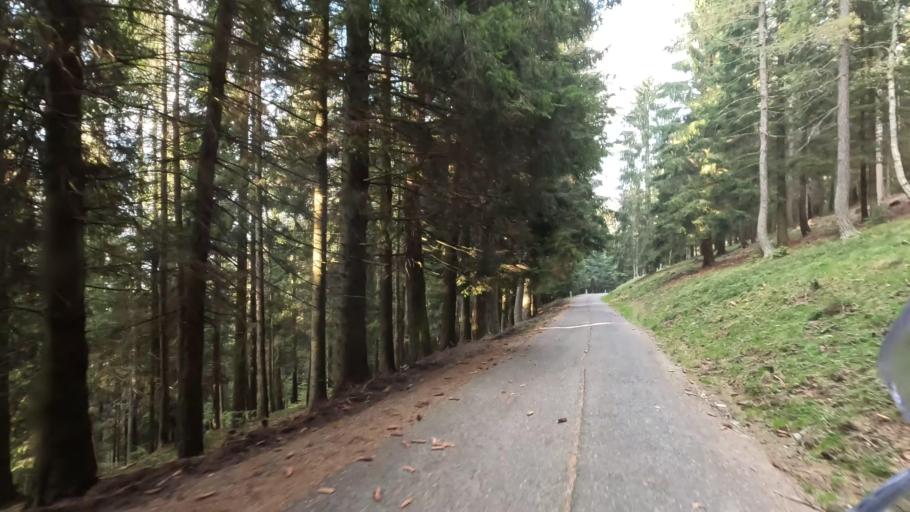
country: IT
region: Lombardy
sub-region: Provincia di Como
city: Pigra
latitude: 45.9831
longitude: 9.1383
